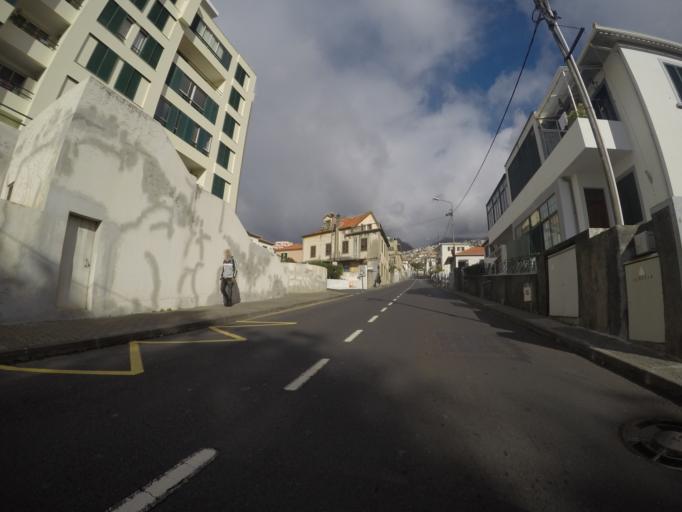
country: PT
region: Madeira
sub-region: Funchal
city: Nossa Senhora do Monte
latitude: 32.6554
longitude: -16.9125
